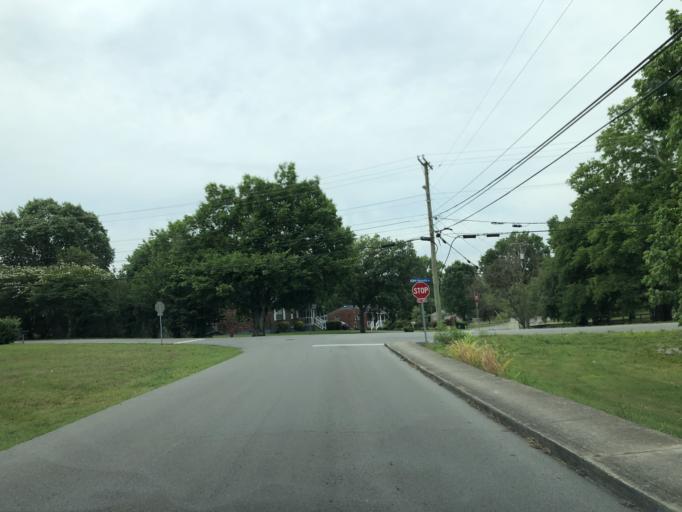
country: US
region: Tennessee
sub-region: Davidson County
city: Goodlettsville
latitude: 36.2887
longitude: -86.7103
